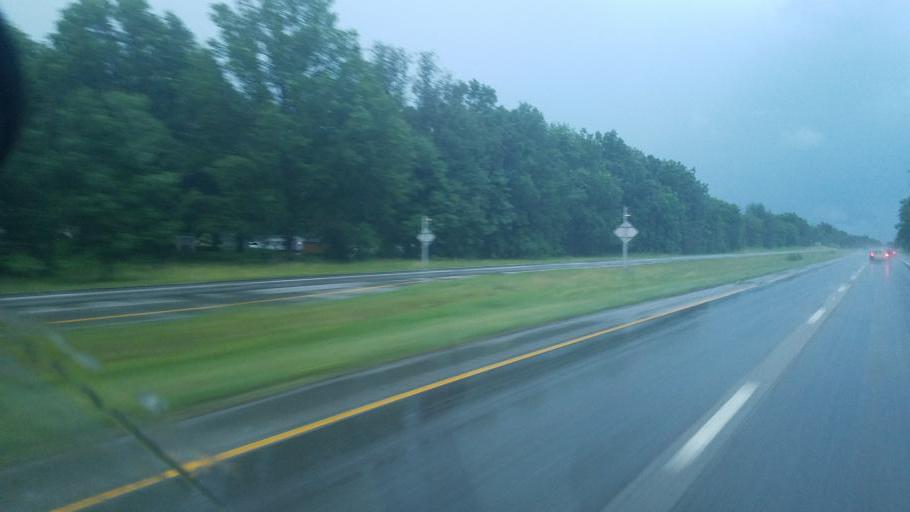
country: US
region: Ohio
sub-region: Wayne County
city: Doylestown
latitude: 40.9579
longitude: -81.6591
